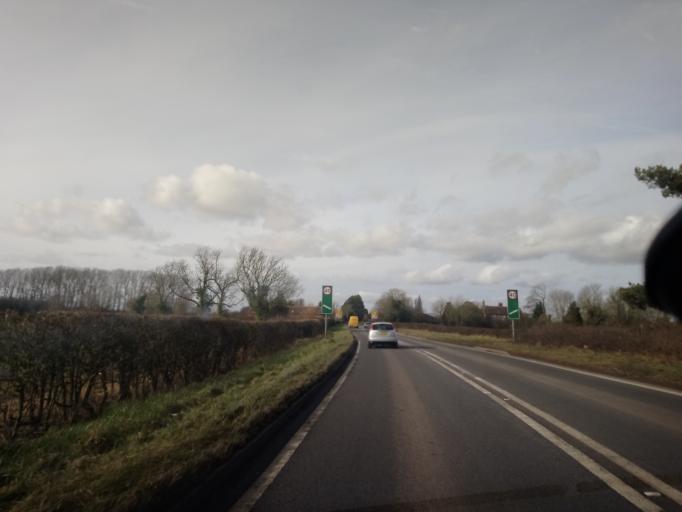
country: GB
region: England
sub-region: Telford and Wrekin
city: Eyton upon the Weald Moors
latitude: 52.7528
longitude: -2.5453
